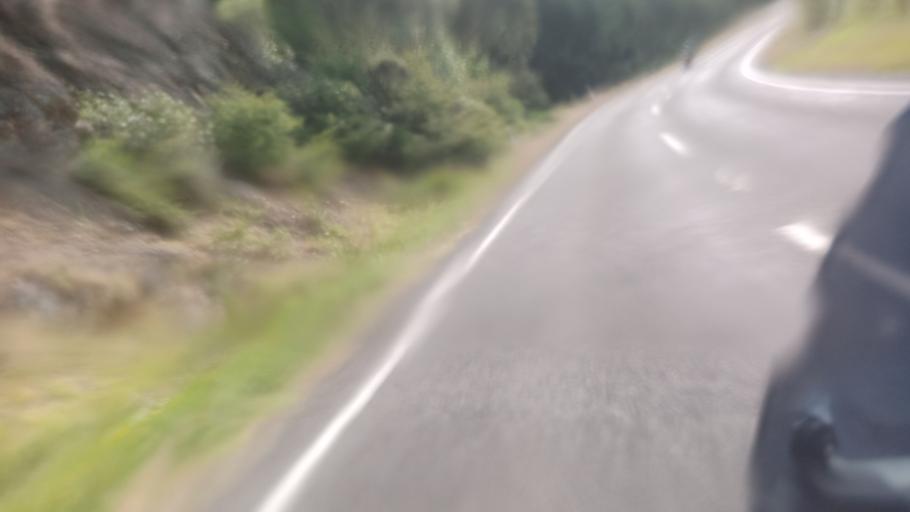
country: NZ
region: Bay of Plenty
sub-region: Opotiki District
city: Opotiki
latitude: -37.6753
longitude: 177.8023
